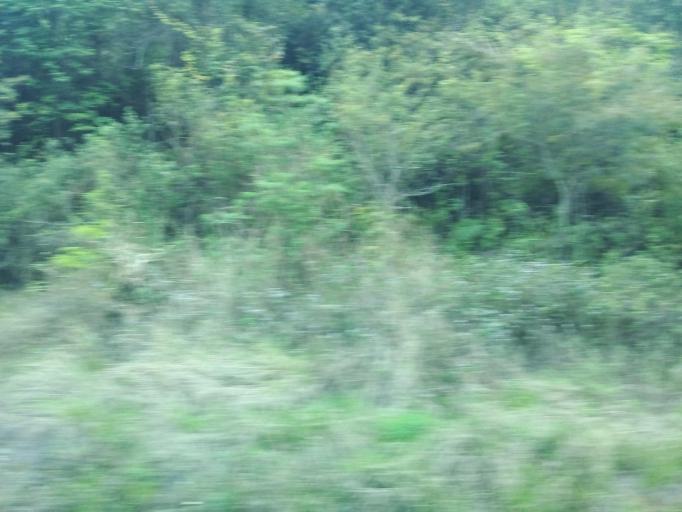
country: BR
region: Minas Gerais
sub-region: Joao Monlevade
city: Joao Monlevade
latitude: -19.8680
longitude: -43.1190
